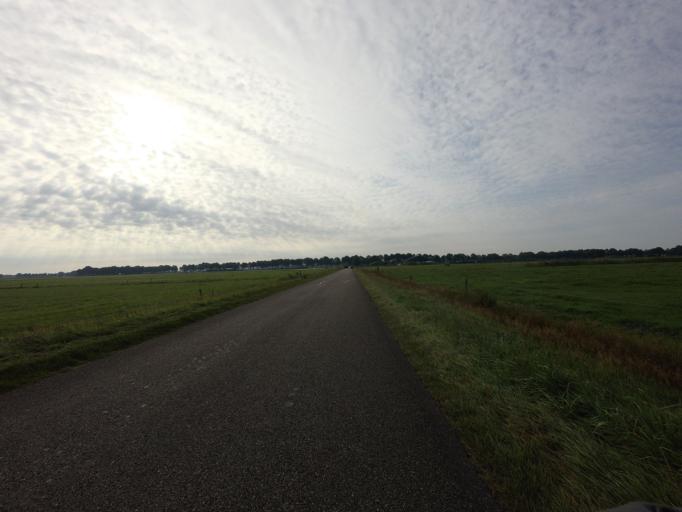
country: NL
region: Friesland
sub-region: Gemeente Weststellingwerf
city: Noordwolde
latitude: 52.9446
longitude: 6.2098
